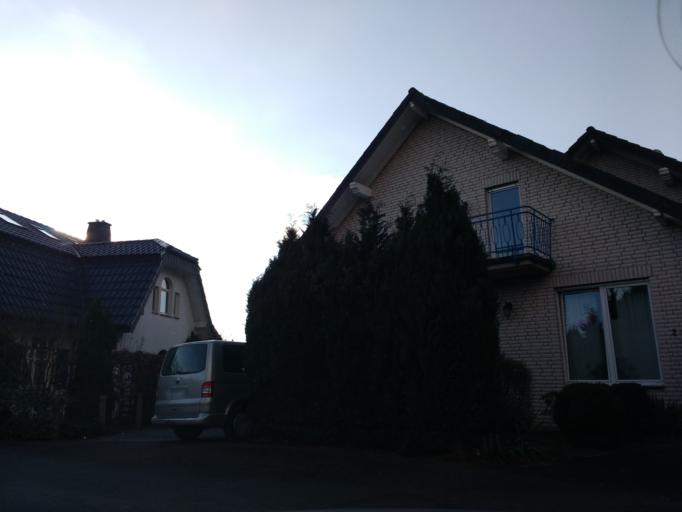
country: DE
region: North Rhine-Westphalia
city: Bad Lippspringe
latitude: 51.7515
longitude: 8.8545
